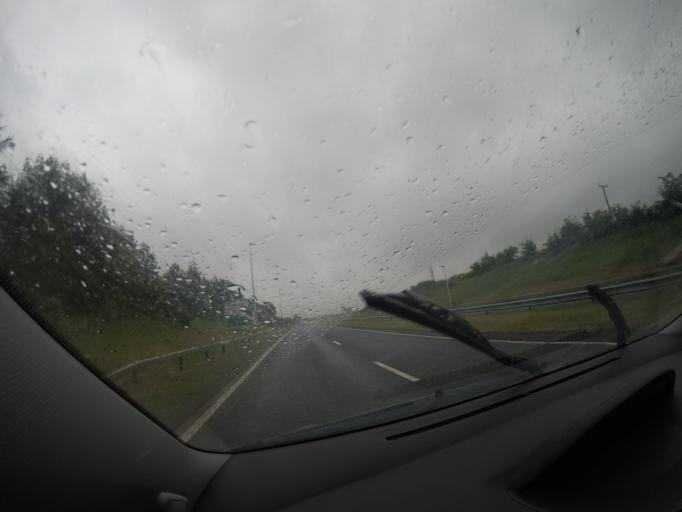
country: GB
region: Scotland
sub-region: Angus
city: Forfar
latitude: 56.6165
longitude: -2.9021
